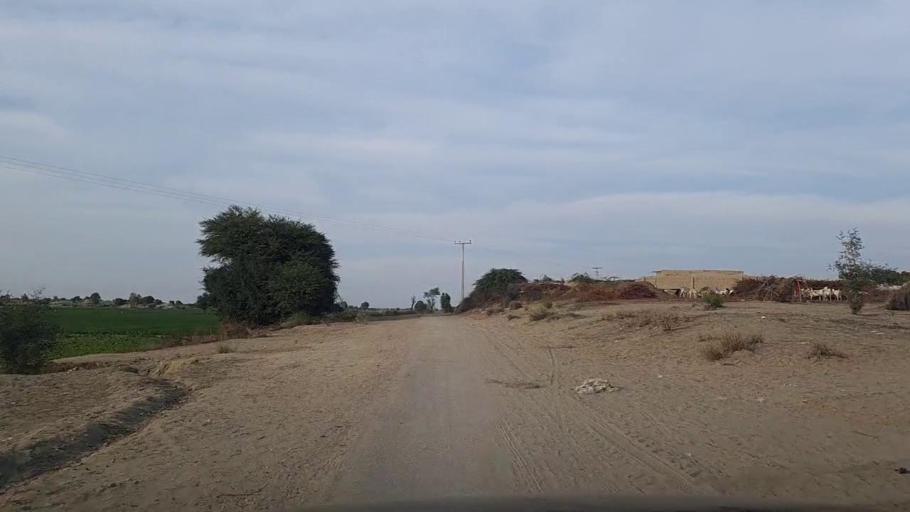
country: PK
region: Sindh
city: Jam Sahib
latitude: 26.4650
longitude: 68.5739
